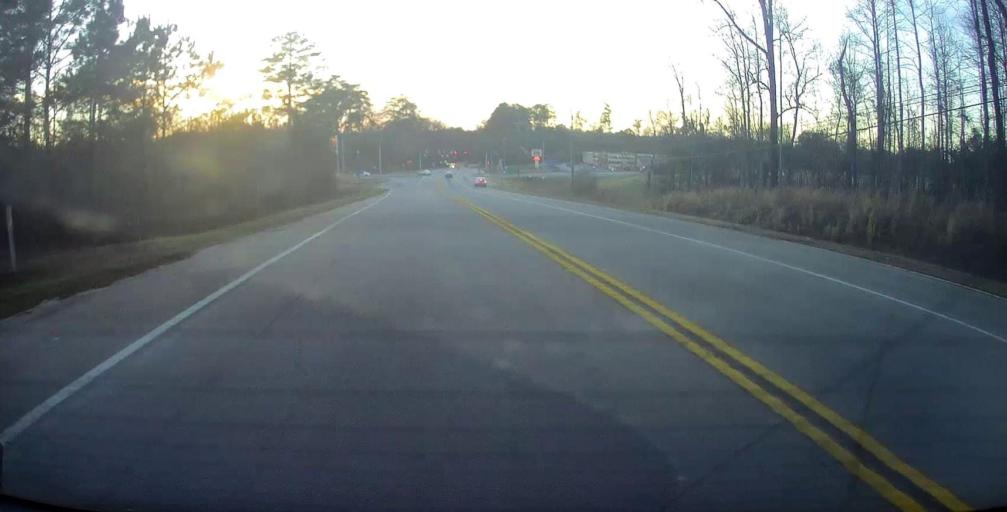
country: US
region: Georgia
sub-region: Troup County
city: La Grange
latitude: 33.0569
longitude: -84.9845
